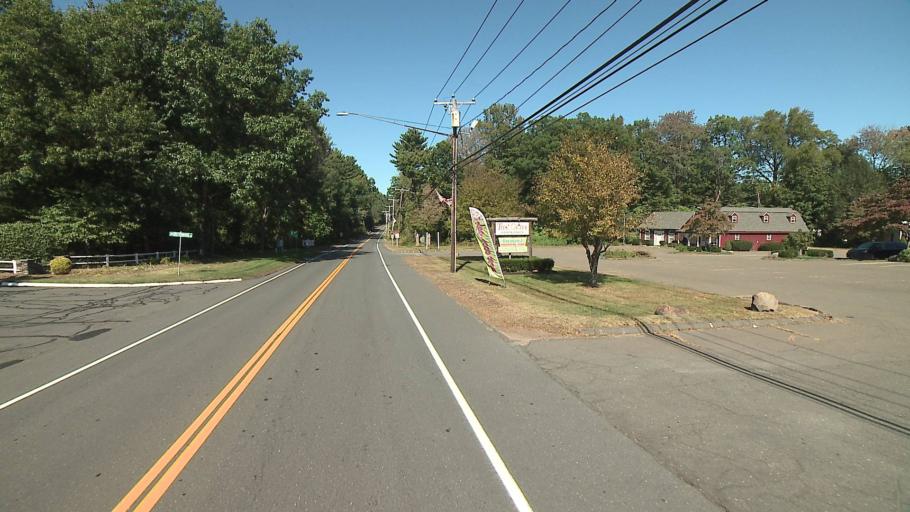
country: US
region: Connecticut
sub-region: Hartford County
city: Tariffville
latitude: 41.9178
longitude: -72.7908
